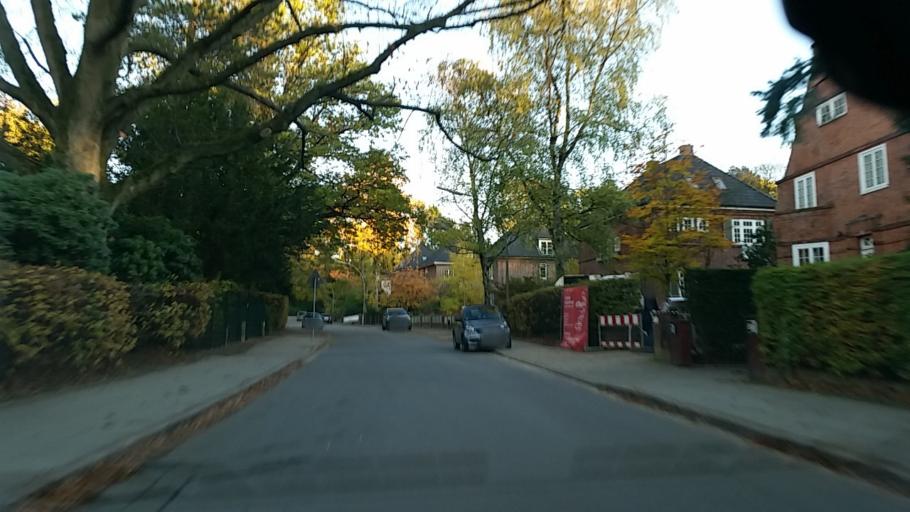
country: DE
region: Schleswig-Holstein
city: Rellingen
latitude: 53.5708
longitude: 9.7942
